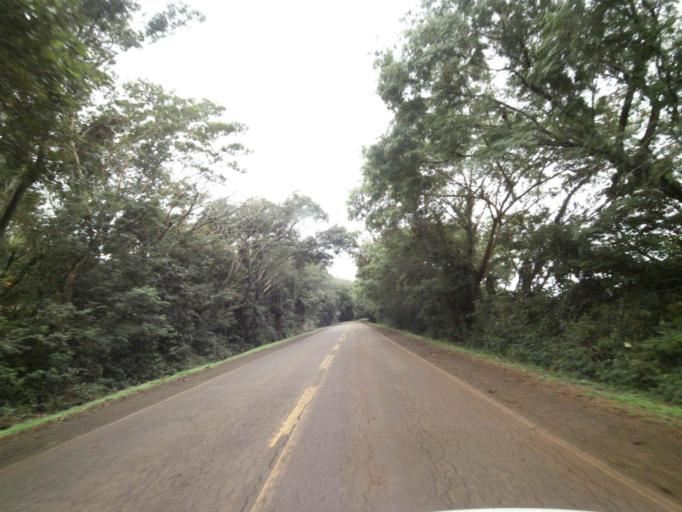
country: BR
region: Parana
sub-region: Marechal Candido Rondon
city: Marechal Candido Rondon
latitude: -24.7953
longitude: -54.2196
